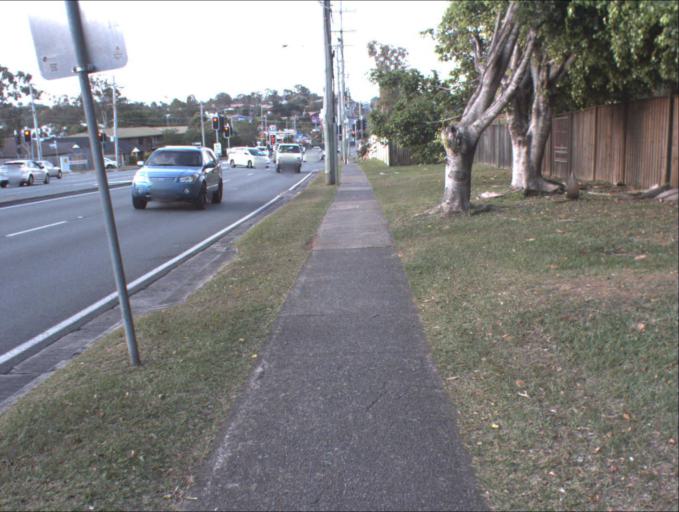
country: AU
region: Queensland
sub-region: Logan
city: Logan City
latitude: -27.6471
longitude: 153.1184
